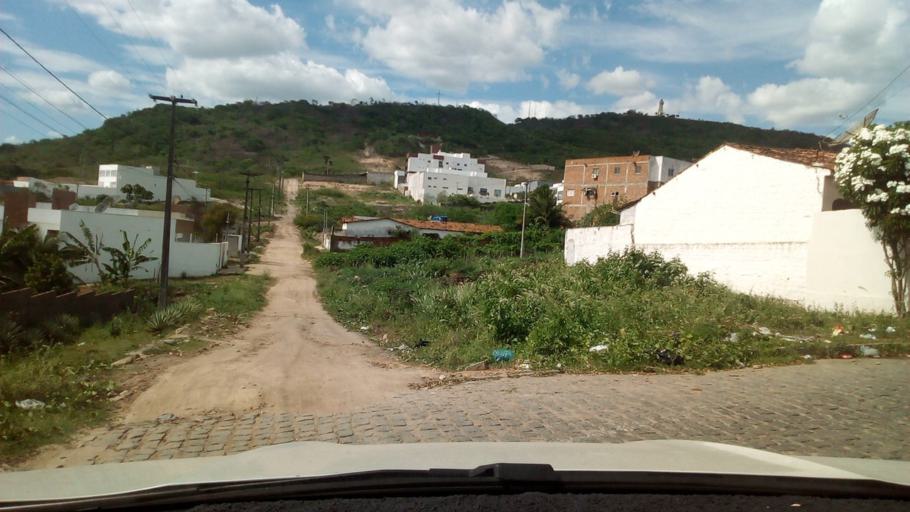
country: BR
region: Paraiba
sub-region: Guarabira
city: Guarabira
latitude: -6.8427
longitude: -35.4956
